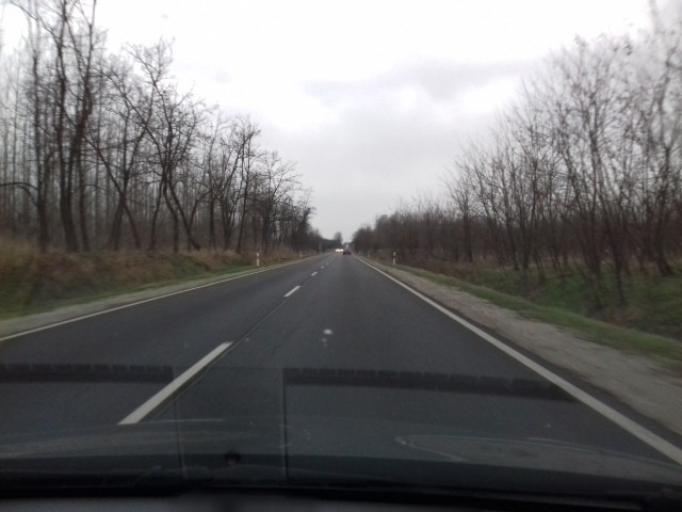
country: HU
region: Szabolcs-Szatmar-Bereg
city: Nyirbogdany
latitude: 48.0375
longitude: 21.8593
